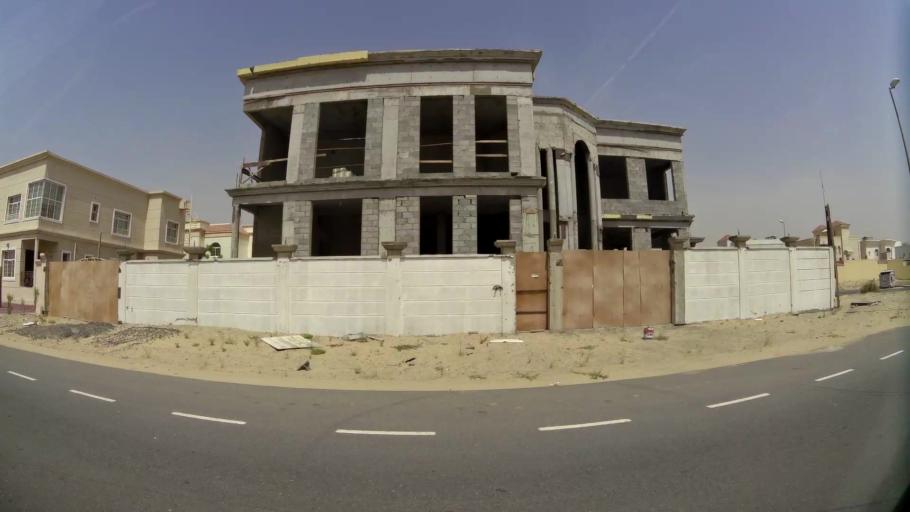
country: AE
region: Ash Shariqah
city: Sharjah
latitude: 25.2642
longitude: 55.4768
